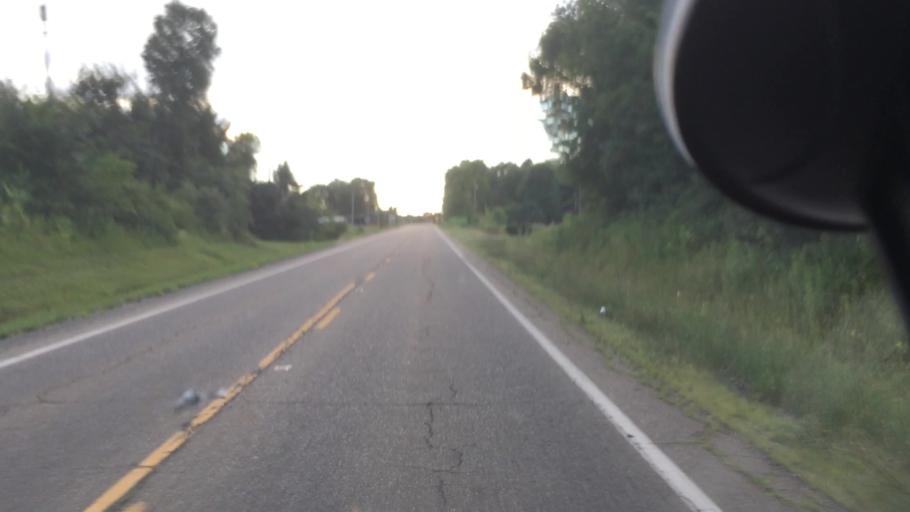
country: US
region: Ohio
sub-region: Columbiana County
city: East Palestine
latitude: 40.8571
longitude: -80.5387
